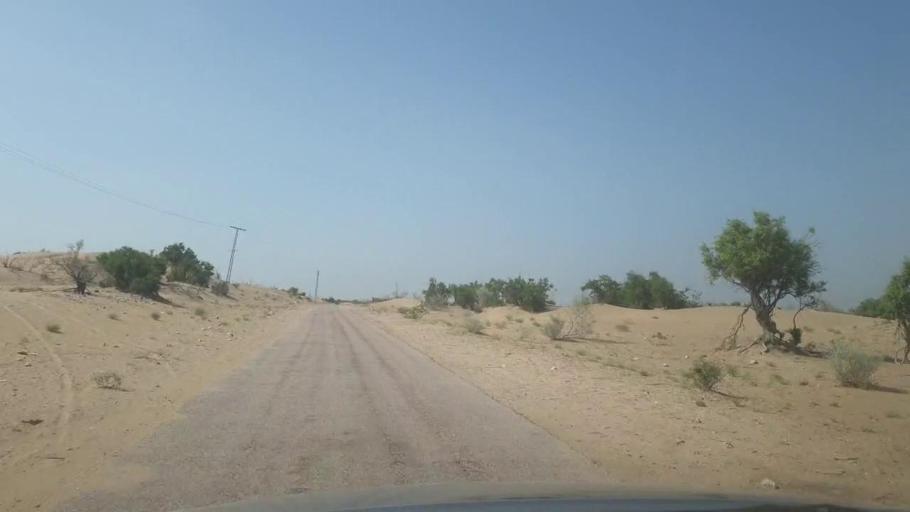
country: PK
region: Sindh
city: Rohri
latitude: 27.4242
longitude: 69.0794
